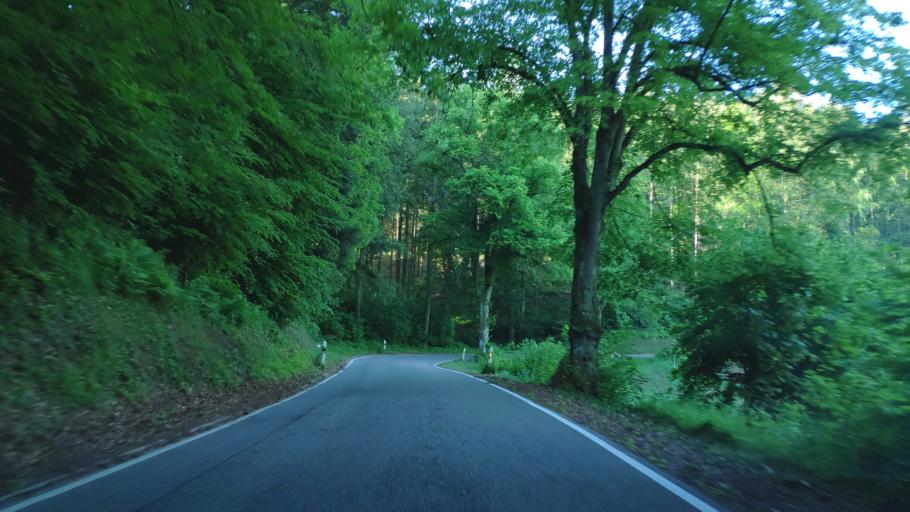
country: DE
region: Rheinland-Pfalz
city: Nothweiler
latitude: 49.0746
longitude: 7.8140
